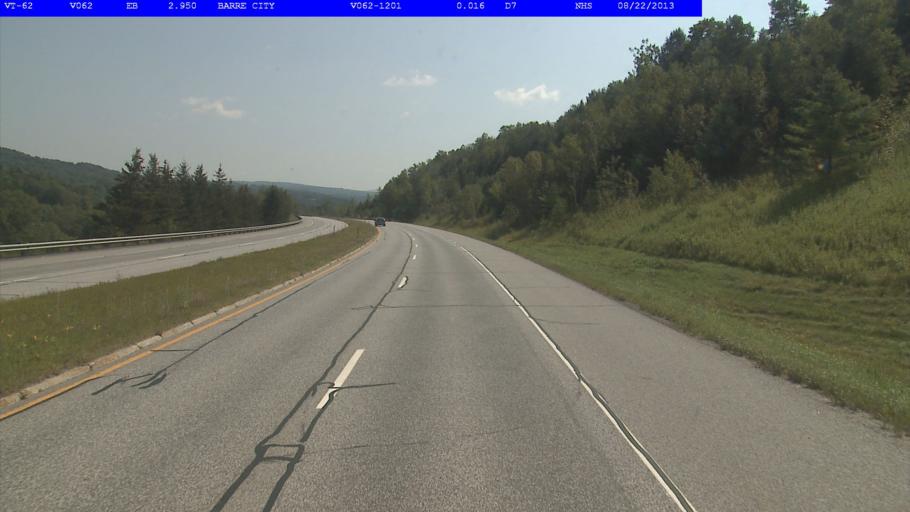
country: US
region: Vermont
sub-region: Washington County
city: Barre
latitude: 44.2125
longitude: -72.5338
